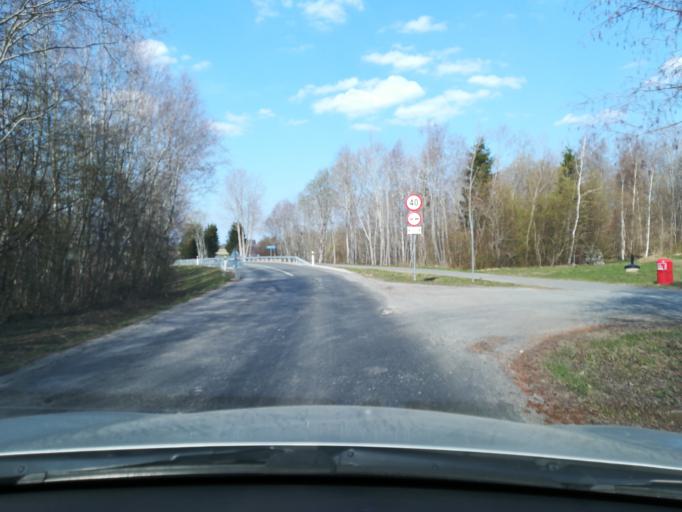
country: EE
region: Harju
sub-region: Saue linn
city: Saue
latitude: 59.3554
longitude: 24.5724
